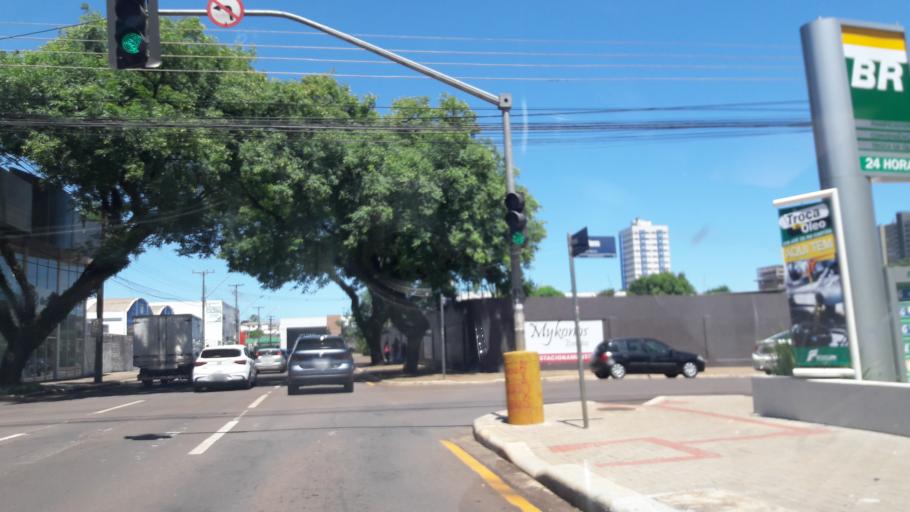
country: BR
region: Parana
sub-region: Cascavel
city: Cascavel
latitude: -24.9535
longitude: -53.4751
